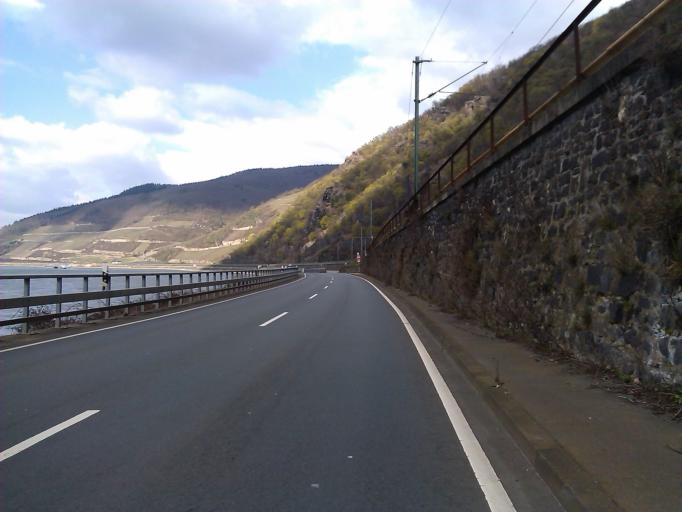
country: DE
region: Rheinland-Pfalz
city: Trechtingshausen
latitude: 50.0048
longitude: 7.8611
